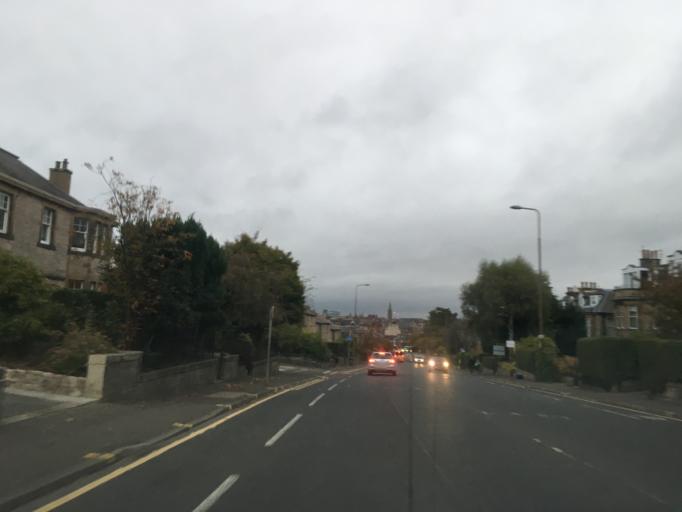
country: GB
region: Scotland
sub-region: Edinburgh
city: Edinburgh
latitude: 55.9262
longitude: -3.1737
